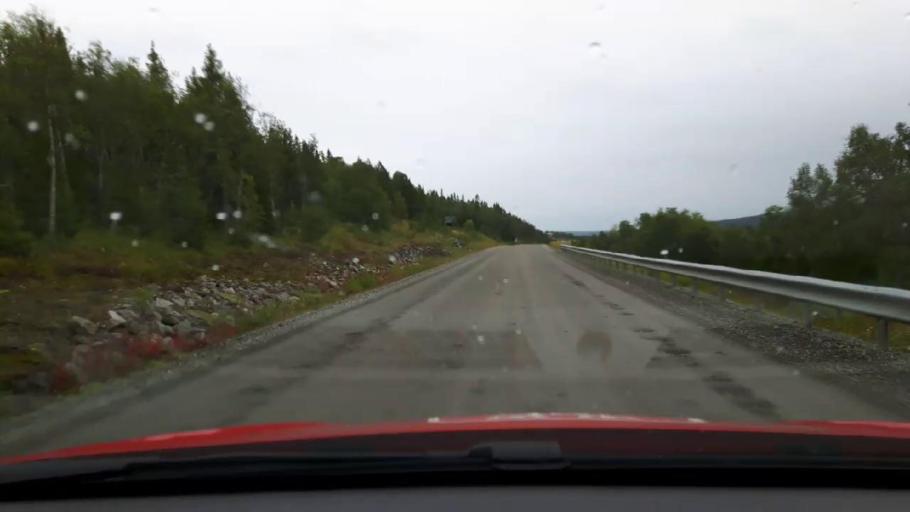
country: NO
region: Nord-Trondelag
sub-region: Meraker
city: Meraker
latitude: 63.5335
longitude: 12.3884
